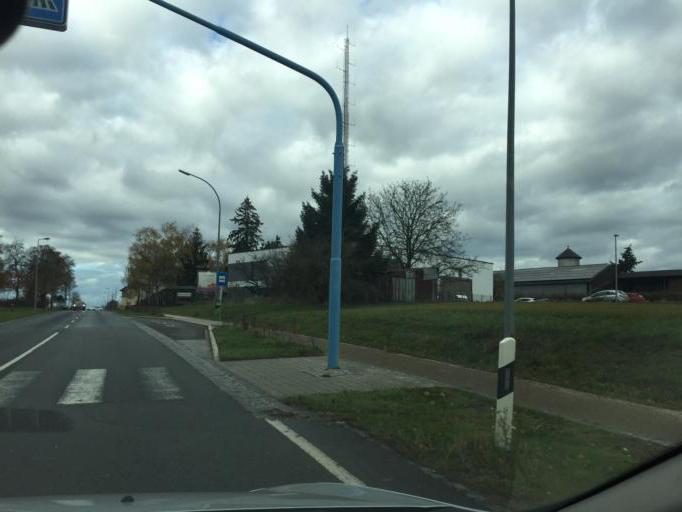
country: LU
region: Diekirch
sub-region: Canton de Wiltz
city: Goesdorf
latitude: 49.8851
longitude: 5.9824
